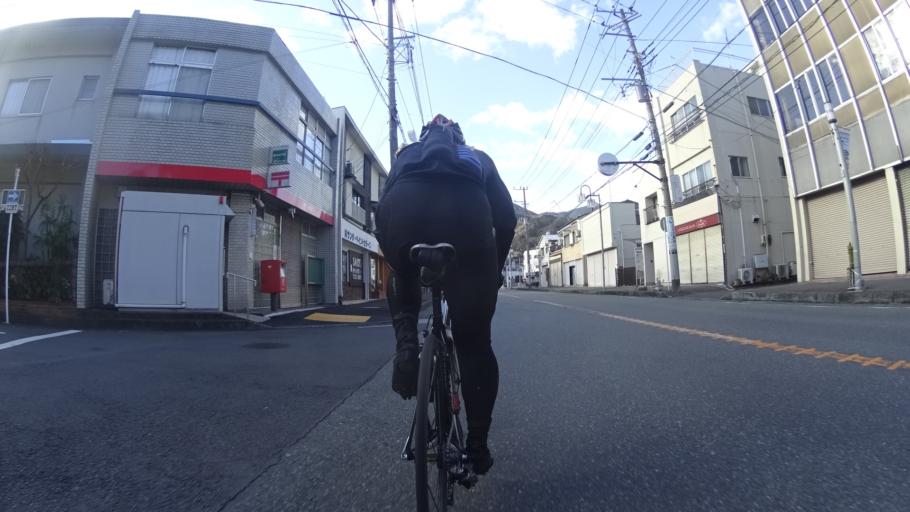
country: JP
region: Kanagawa
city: Yugawara
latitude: 35.1439
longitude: 139.0999
